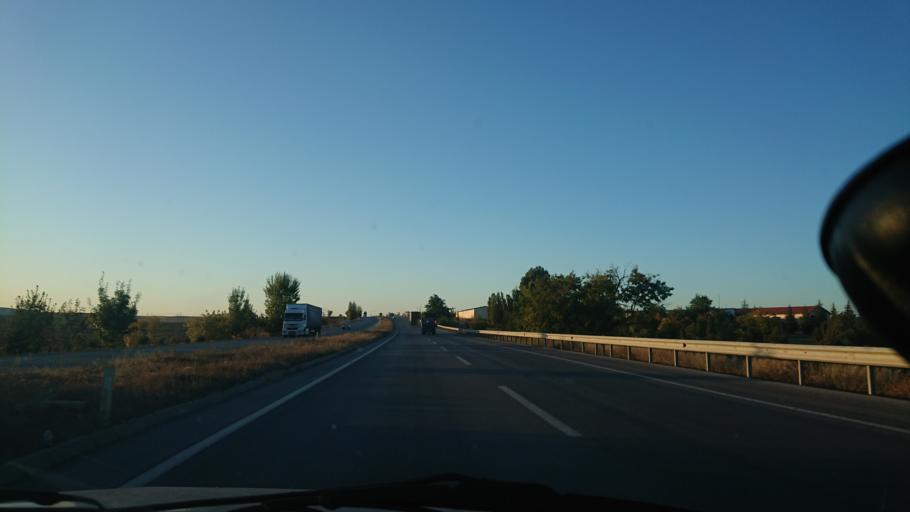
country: TR
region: Eskisehir
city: Mahmudiye
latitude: 39.4809
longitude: 30.9885
